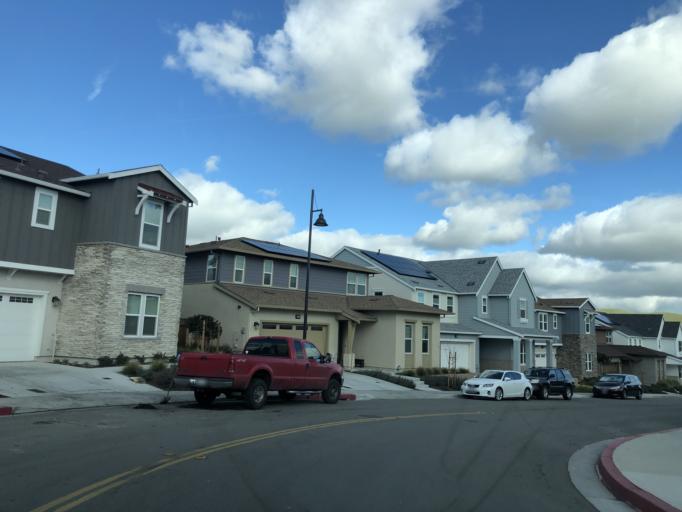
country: US
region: California
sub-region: Alameda County
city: Dublin
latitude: 37.7374
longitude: -121.8809
